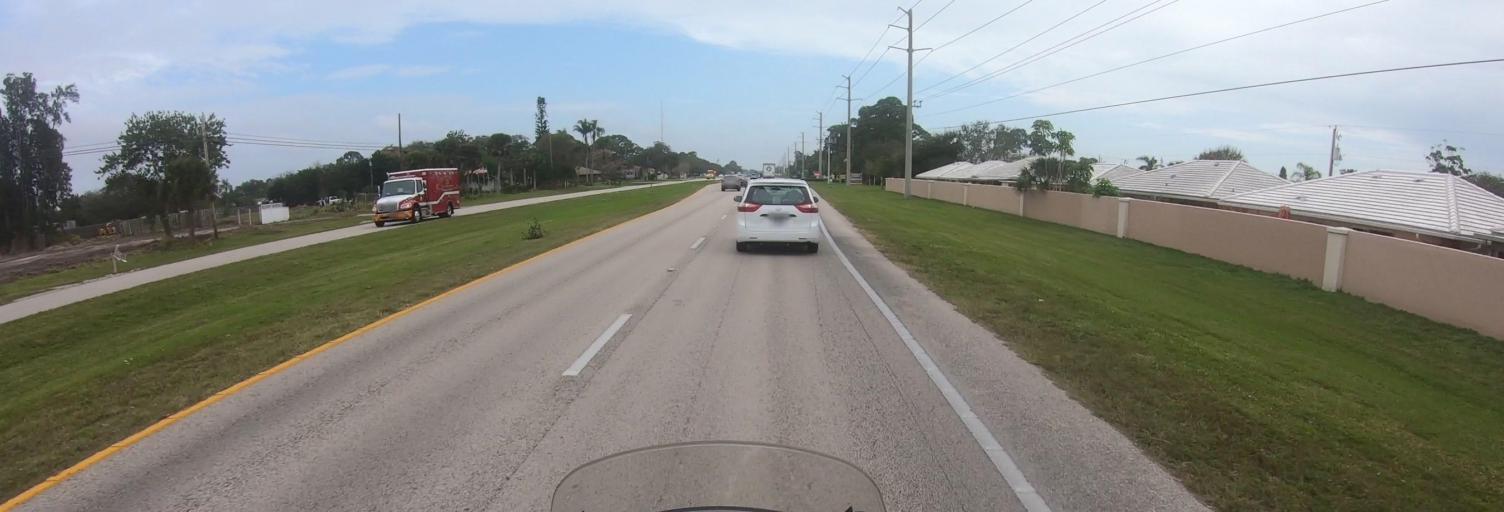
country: US
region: Florida
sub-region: Sarasota County
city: Laurel
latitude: 27.1629
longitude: -82.4752
